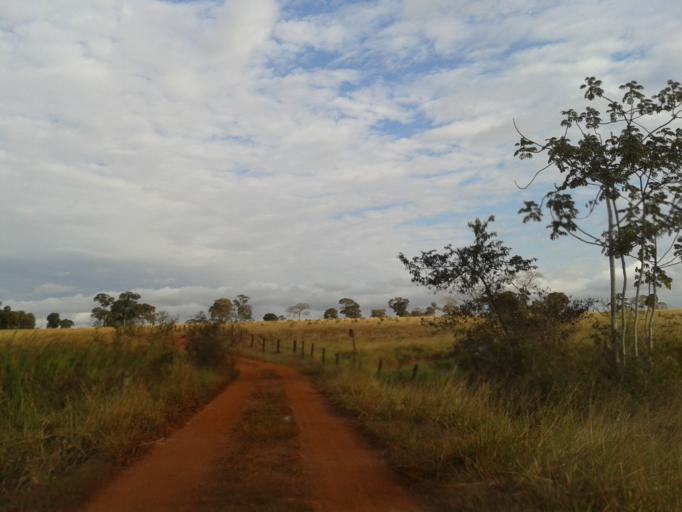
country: BR
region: Minas Gerais
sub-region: Santa Vitoria
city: Santa Vitoria
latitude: -18.7339
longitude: -50.2357
